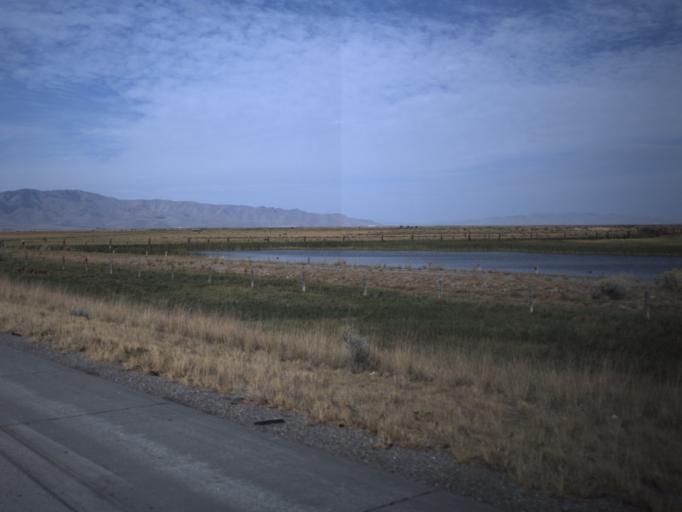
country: US
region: Utah
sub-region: Tooele County
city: Stansbury park
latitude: 40.6682
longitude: -112.3038
